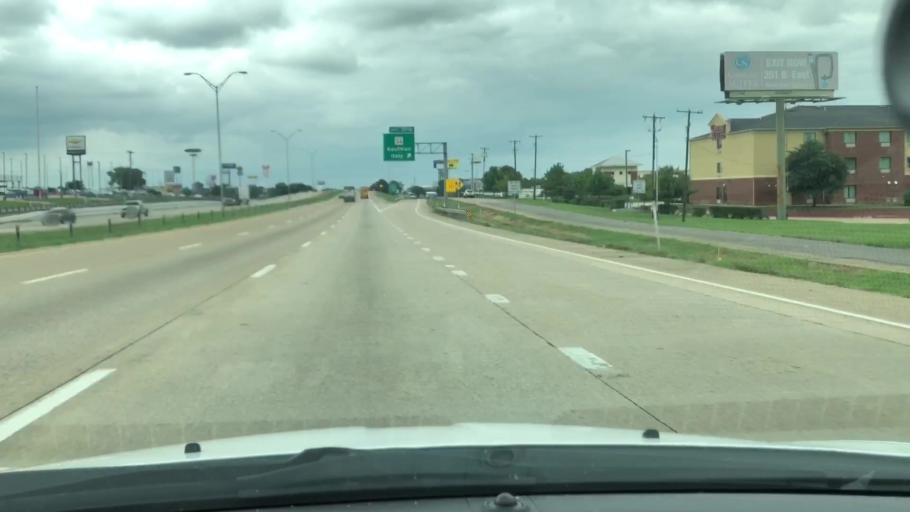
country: US
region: Texas
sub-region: Ellis County
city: Ennis
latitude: 32.3299
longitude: -96.6123
